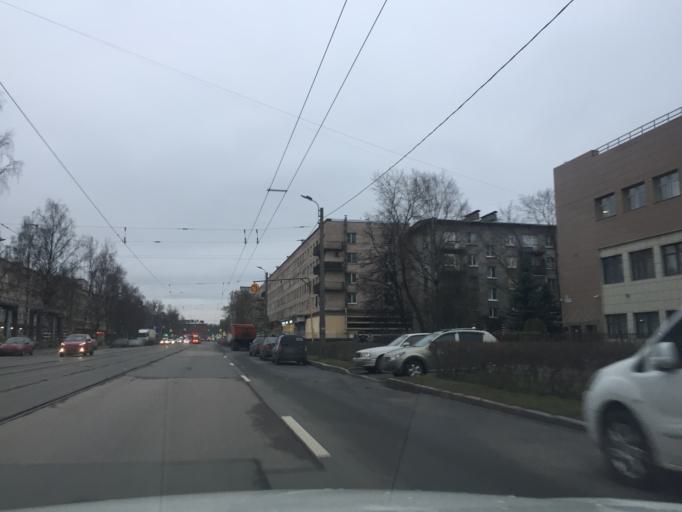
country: RU
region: St.-Petersburg
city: Sosnovka
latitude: 60.0155
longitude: 30.3678
